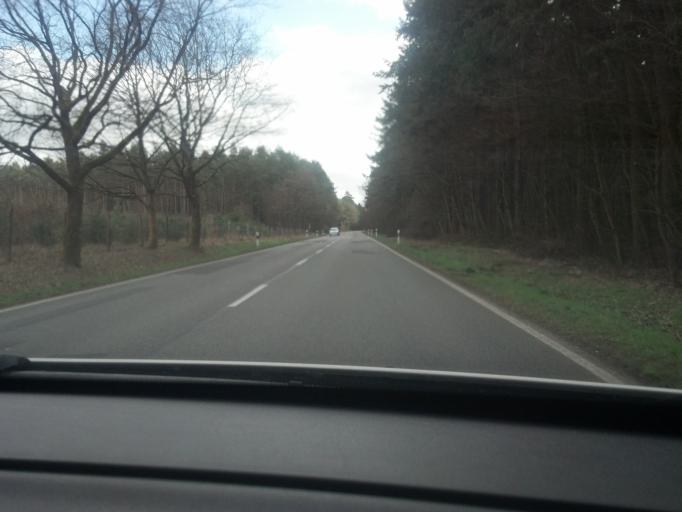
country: DE
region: Mecklenburg-Vorpommern
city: Plau am See
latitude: 53.3833
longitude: 12.3180
